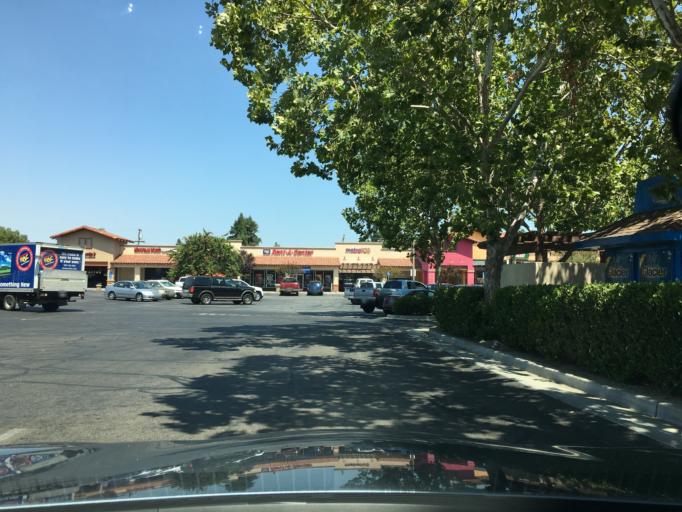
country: US
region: California
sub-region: Santa Clara County
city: Gilroy
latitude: 37.0137
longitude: -121.5835
